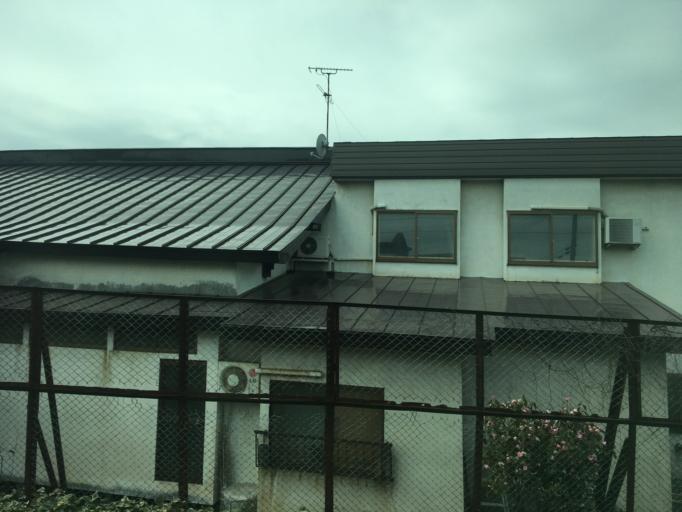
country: JP
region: Aomori
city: Hirosaki
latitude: 40.6059
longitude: 140.4835
